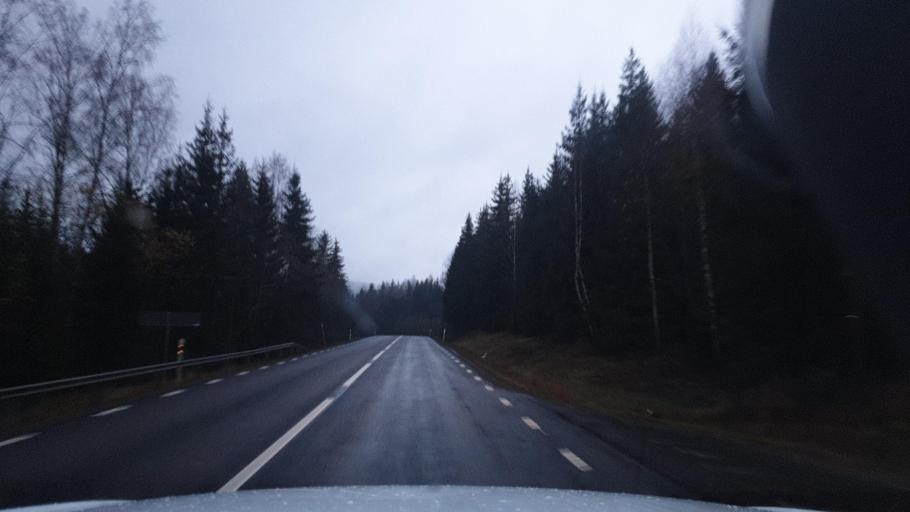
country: SE
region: Vaermland
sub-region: Eda Kommun
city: Amotfors
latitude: 59.8140
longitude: 12.3220
